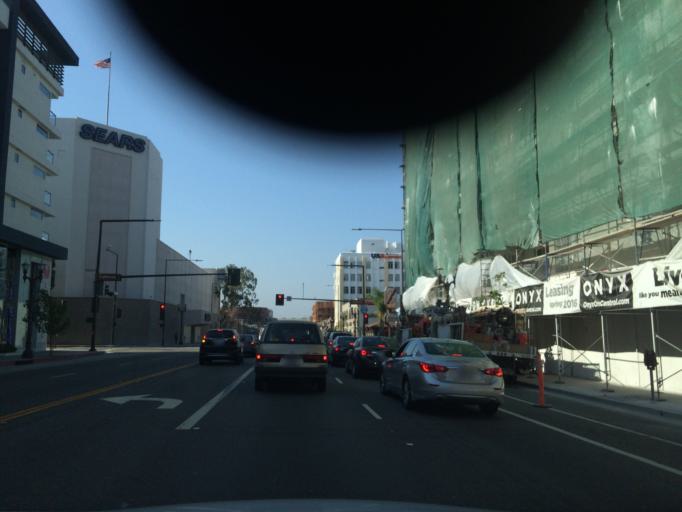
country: US
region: California
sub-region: Los Angeles County
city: Glendale
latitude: 34.1504
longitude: -118.2580
